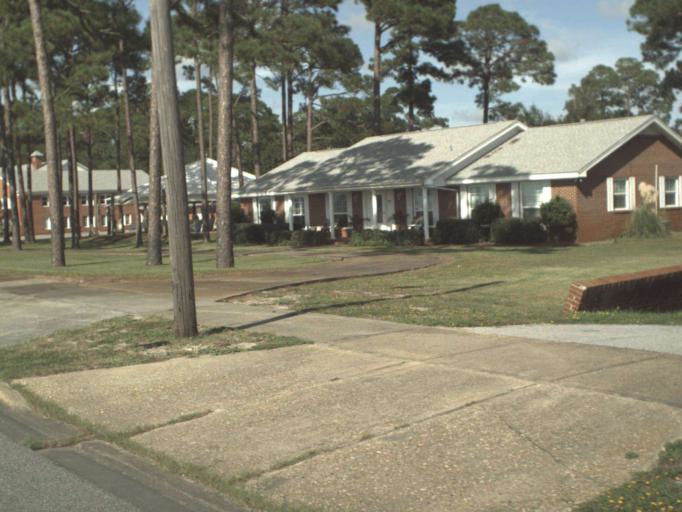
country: US
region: Florida
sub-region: Gulf County
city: Port Saint Joe
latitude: 29.8047
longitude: -85.3018
